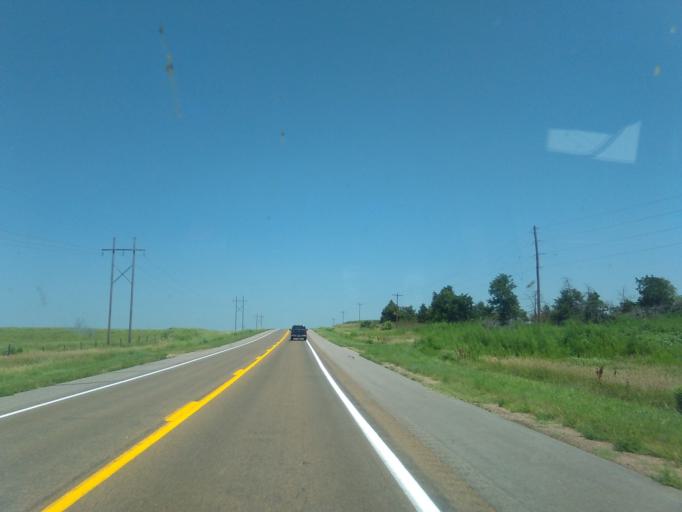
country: US
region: Nebraska
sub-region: Lincoln County
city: North Platte
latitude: 40.8001
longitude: -100.7537
